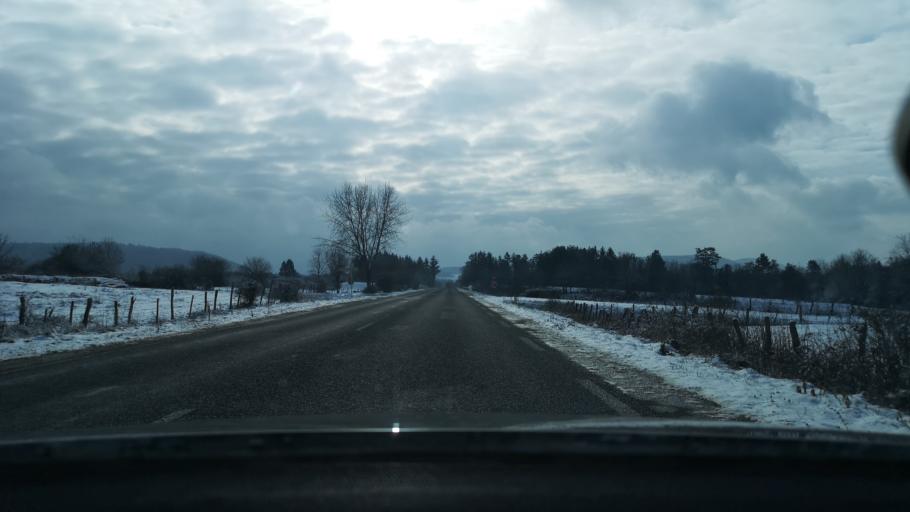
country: FR
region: Franche-Comte
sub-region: Departement du Jura
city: Orgelet
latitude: 46.5545
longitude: 5.5963
